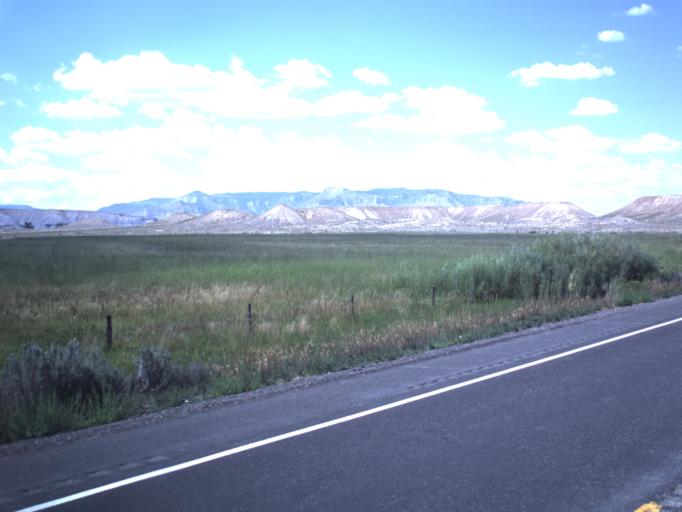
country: US
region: Utah
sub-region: Emery County
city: Huntington
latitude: 39.2756
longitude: -110.9771
